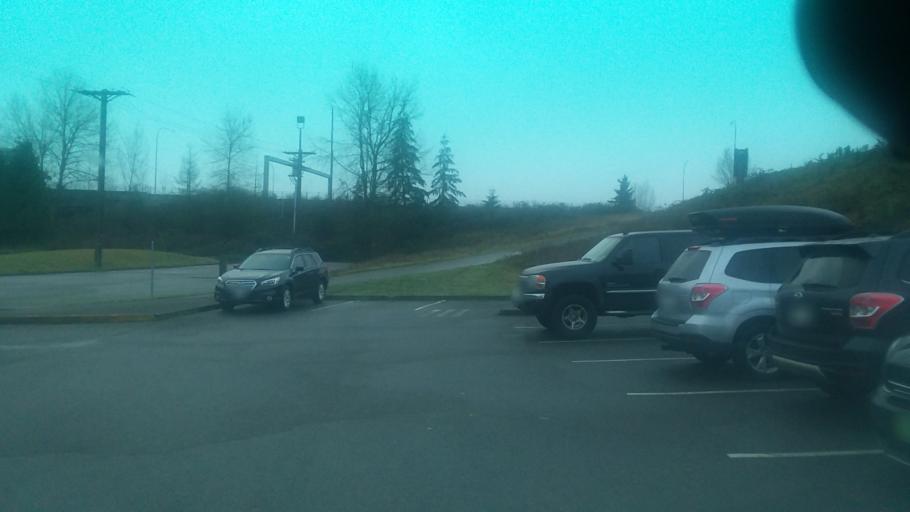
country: US
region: Washington
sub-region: Pierce County
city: Tacoma
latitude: 47.2364
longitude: -122.4767
